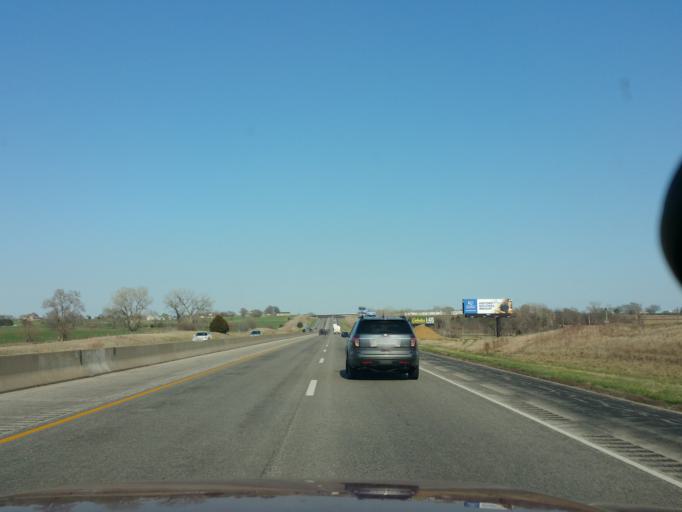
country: US
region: Kansas
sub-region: Leavenworth County
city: Basehor
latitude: 39.0803
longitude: -94.9605
